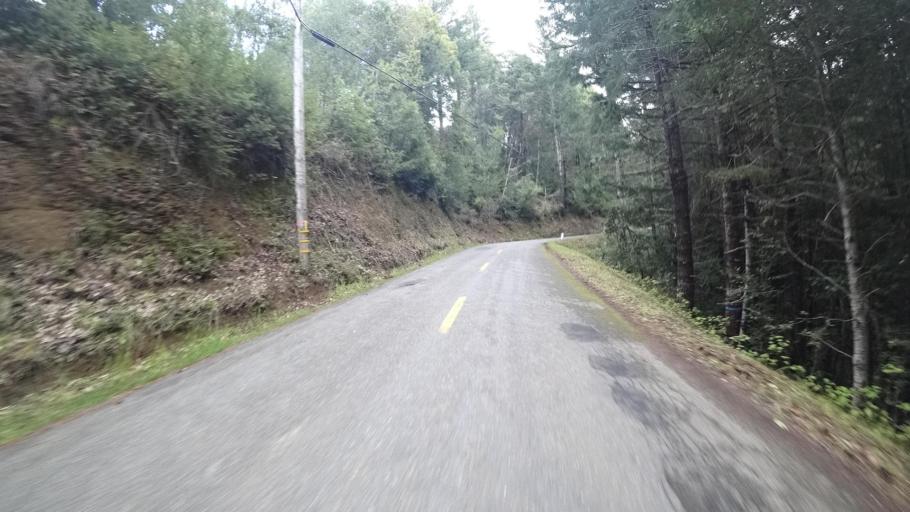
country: US
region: California
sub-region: Humboldt County
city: Bayside
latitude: 40.7505
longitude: -123.9725
